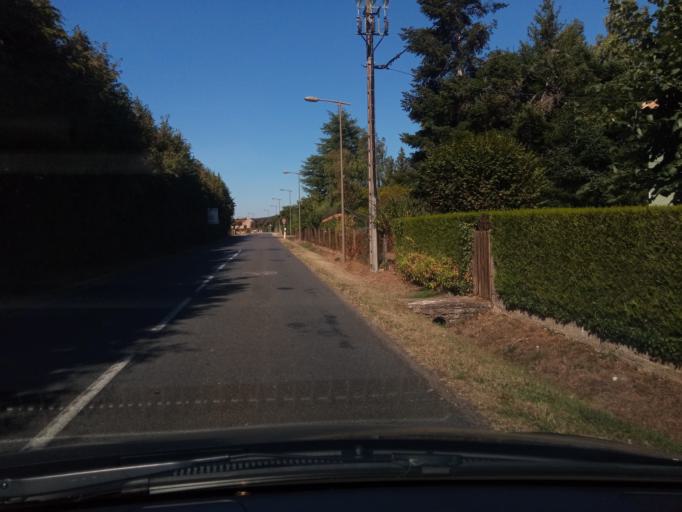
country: FR
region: Poitou-Charentes
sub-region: Departement de la Vienne
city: Montmorillon
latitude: 46.4883
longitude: 0.8439
